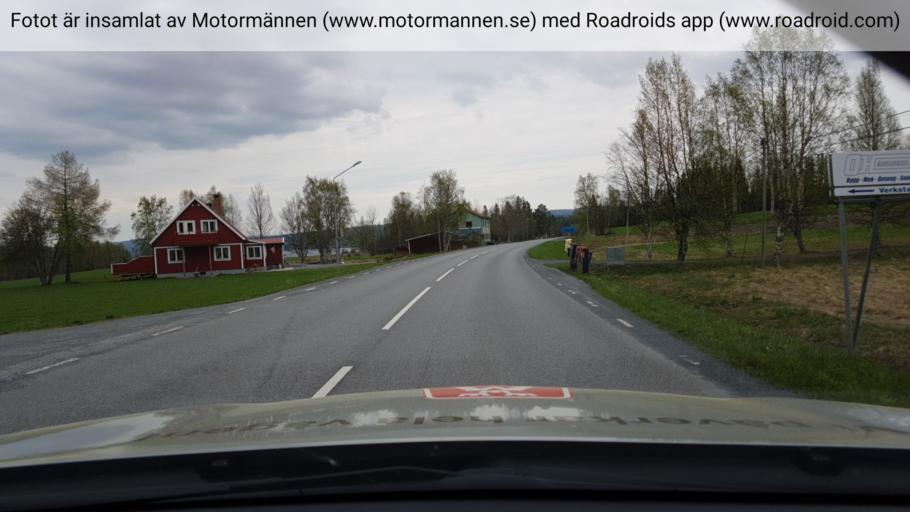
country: SE
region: Jaemtland
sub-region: Are Kommun
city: Jarpen
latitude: 63.4109
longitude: 13.3662
